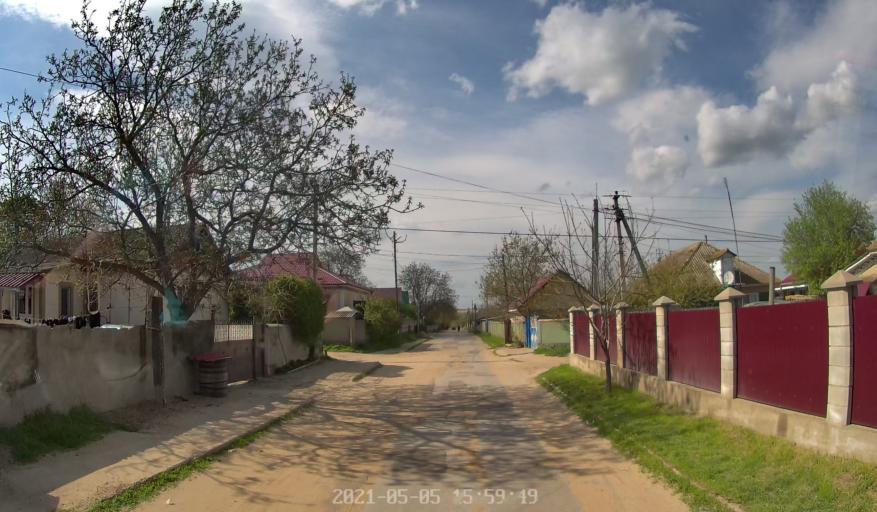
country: MD
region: Criuleni
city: Criuleni
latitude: 47.1416
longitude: 29.2015
